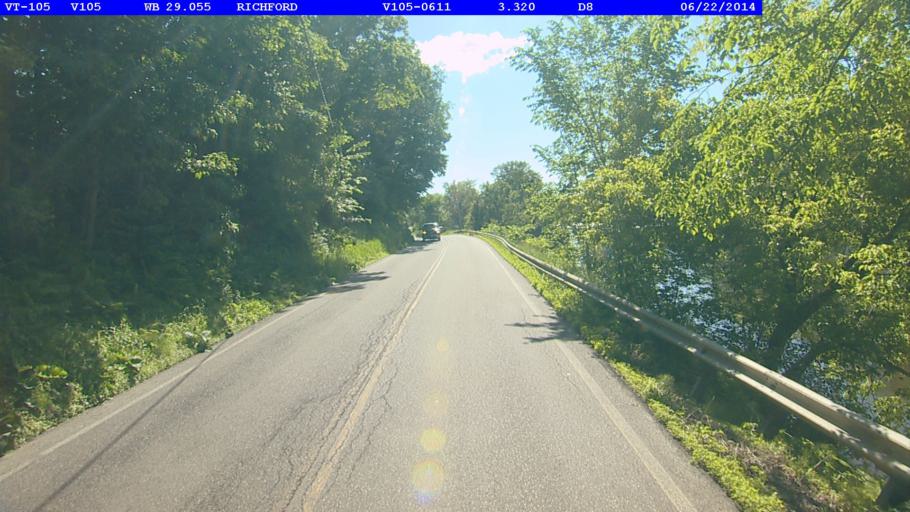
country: US
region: Vermont
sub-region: Franklin County
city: Richford
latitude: 44.9874
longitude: -72.6521
